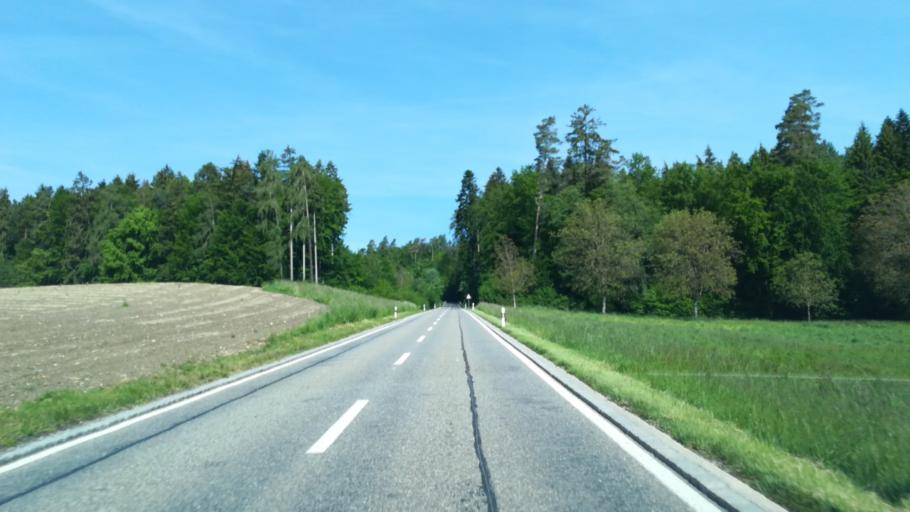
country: CH
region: Thurgau
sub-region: Frauenfeld District
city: Pfyn
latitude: 47.6057
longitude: 8.9407
